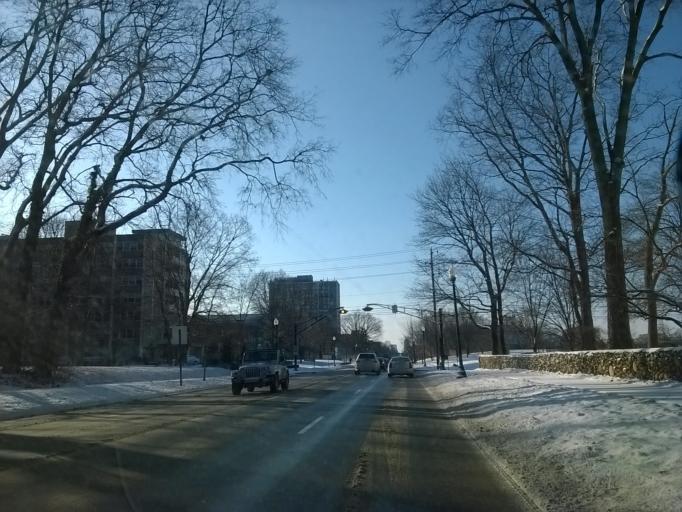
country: US
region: Indiana
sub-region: Marion County
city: Broad Ripple
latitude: 39.8289
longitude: -86.1570
